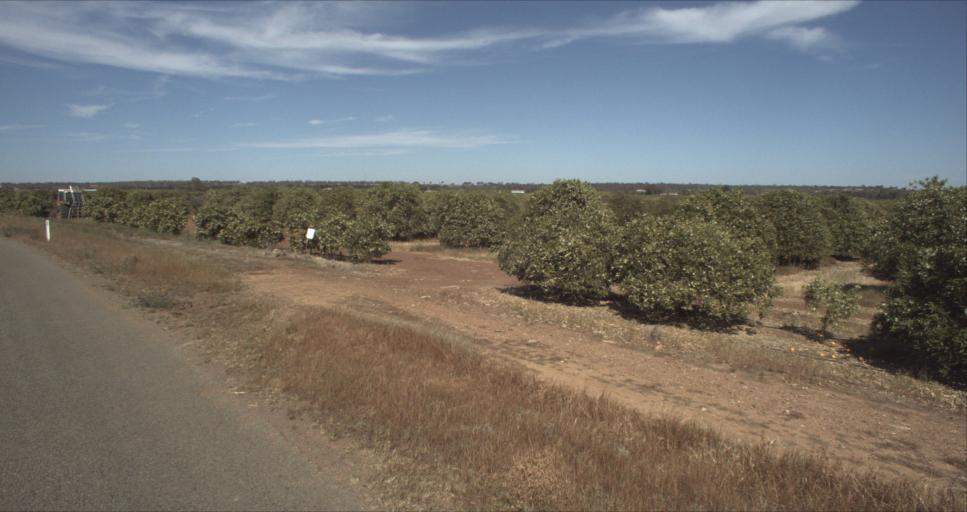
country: AU
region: New South Wales
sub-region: Leeton
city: Leeton
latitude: -34.5800
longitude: 146.4775
